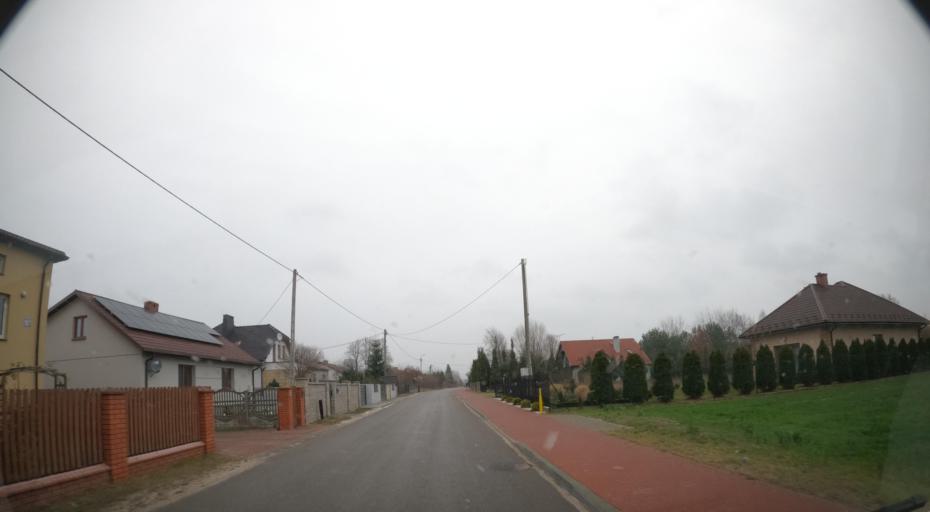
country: PL
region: Masovian Voivodeship
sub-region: Powiat radomski
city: Jedlnia-Letnisko
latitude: 51.4157
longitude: 21.2658
